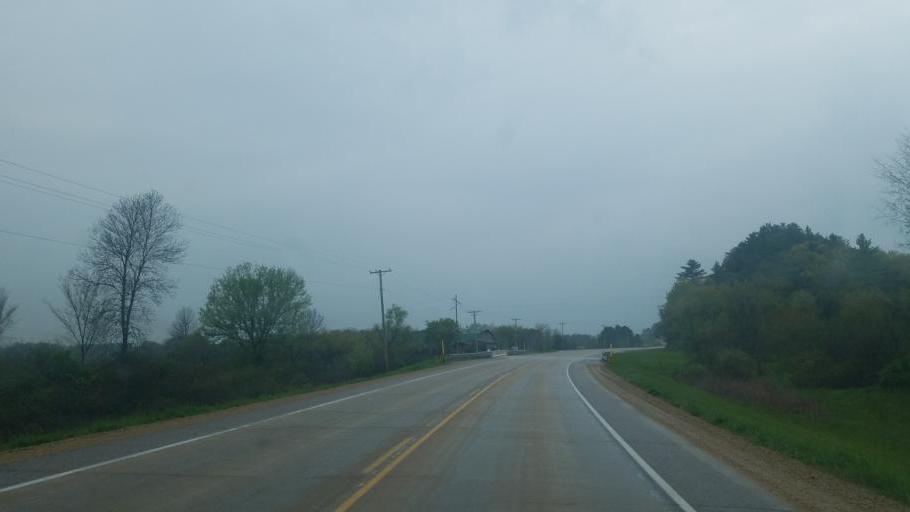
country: US
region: Wisconsin
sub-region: Juneau County
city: Elroy
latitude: 43.6260
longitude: -90.1679
